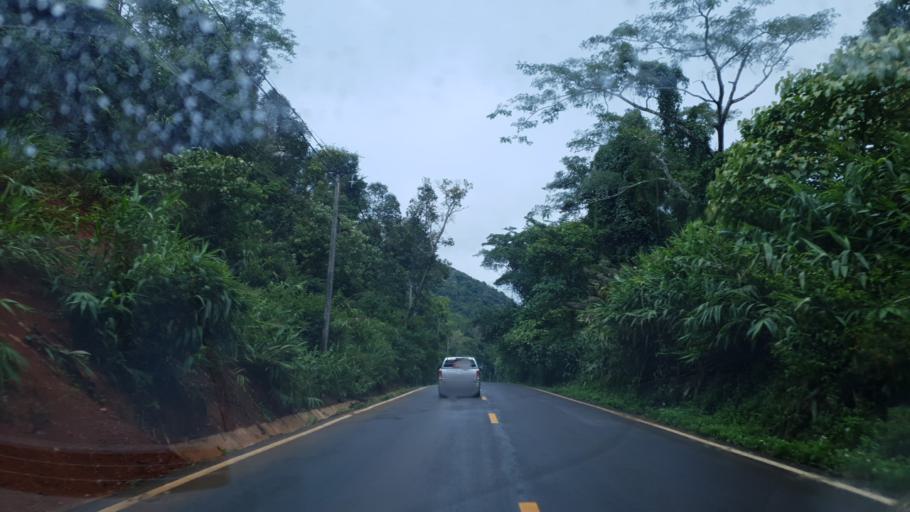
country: TH
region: Mae Hong Son
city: Ban Huai I Huak
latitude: 18.1494
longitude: 98.0969
